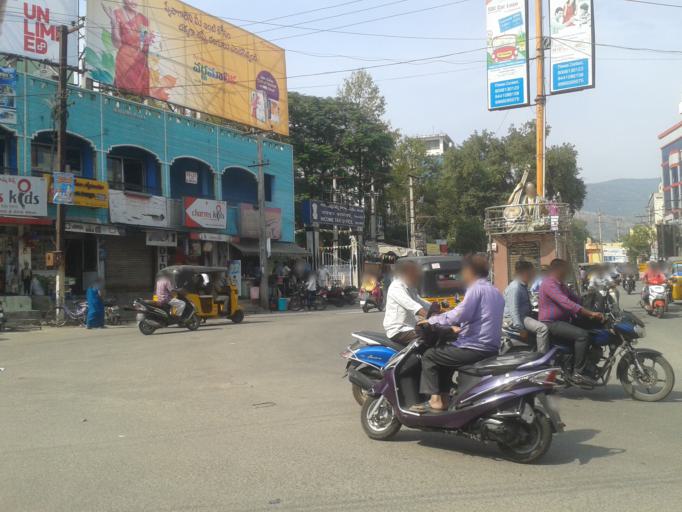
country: IN
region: Andhra Pradesh
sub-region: Chittoor
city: Tirupati
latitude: 13.6371
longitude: 79.4187
